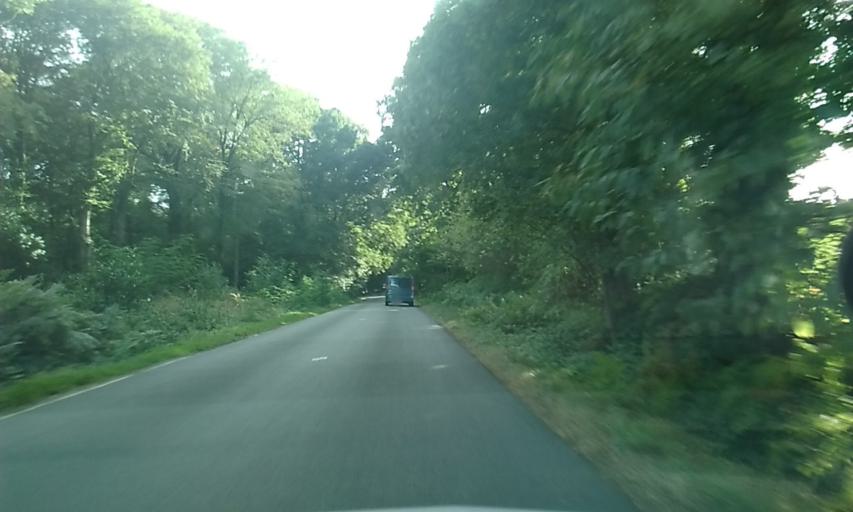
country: FR
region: Brittany
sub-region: Departement d'Ille-et-Vilaine
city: Iffendic
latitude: 48.1617
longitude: -2.0125
